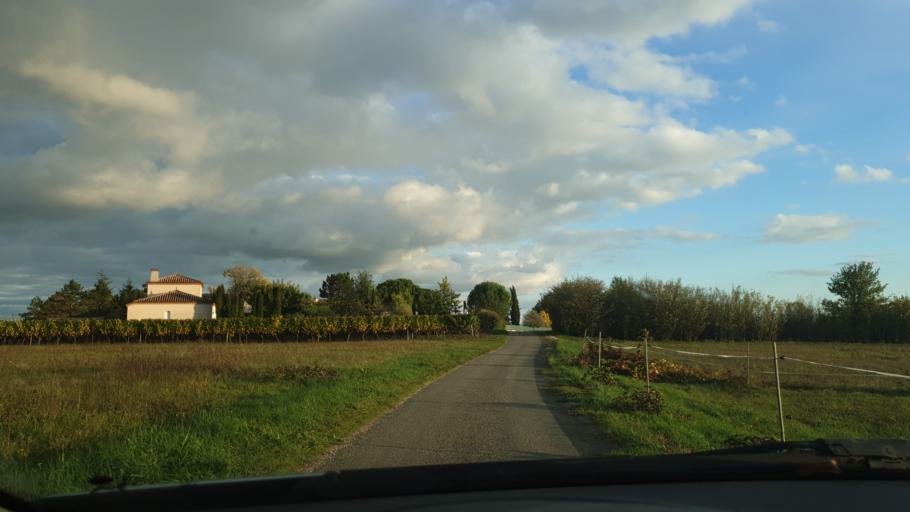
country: FR
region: Midi-Pyrenees
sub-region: Departement du Lot
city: Luzech
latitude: 44.4157
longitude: 1.2518
